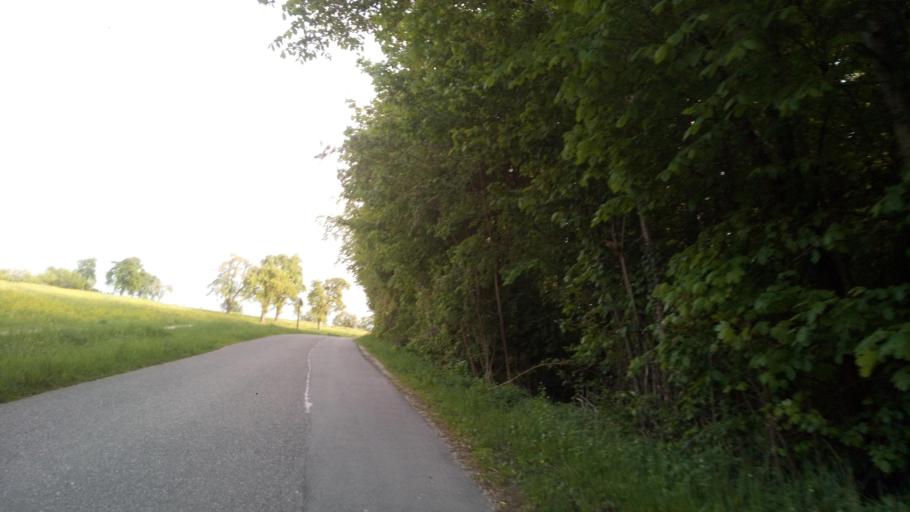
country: DE
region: Baden-Wuerttemberg
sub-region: Regierungsbezirk Stuttgart
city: Salach
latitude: 48.7011
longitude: 9.7508
